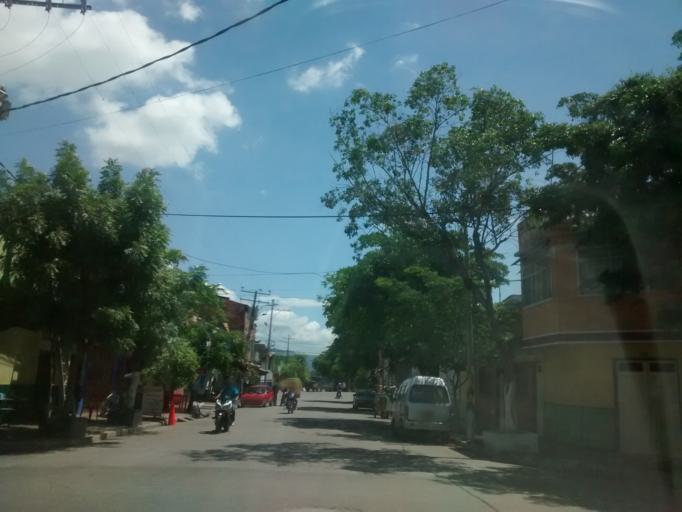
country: CO
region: Cundinamarca
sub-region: Girardot
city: Girardot City
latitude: 4.2982
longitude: -74.8001
